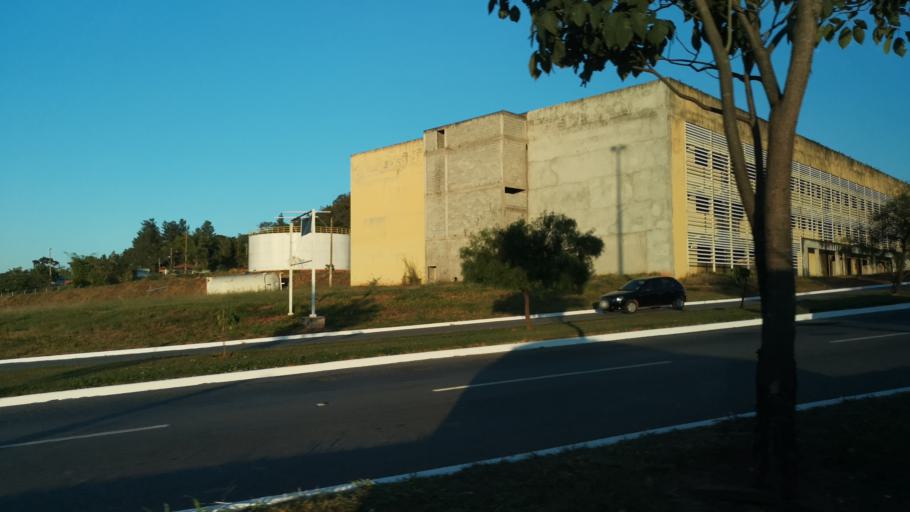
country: BR
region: Goias
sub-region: Senador Canedo
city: Senador Canedo
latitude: -16.6817
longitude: -49.1175
